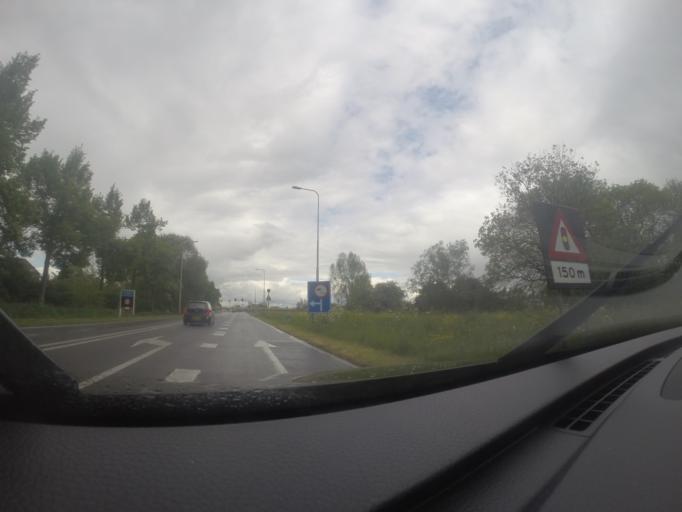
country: NL
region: Gelderland
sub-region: Gemeente Zutphen
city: Zutphen
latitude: 52.1393
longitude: 6.1838
